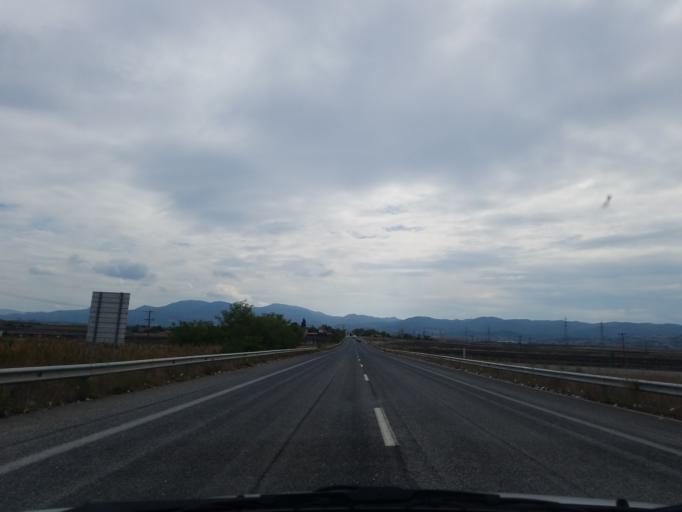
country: GR
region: Central Greece
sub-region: Nomos Fthiotidos
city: Omvriaki
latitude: 39.0818
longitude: 22.3112
